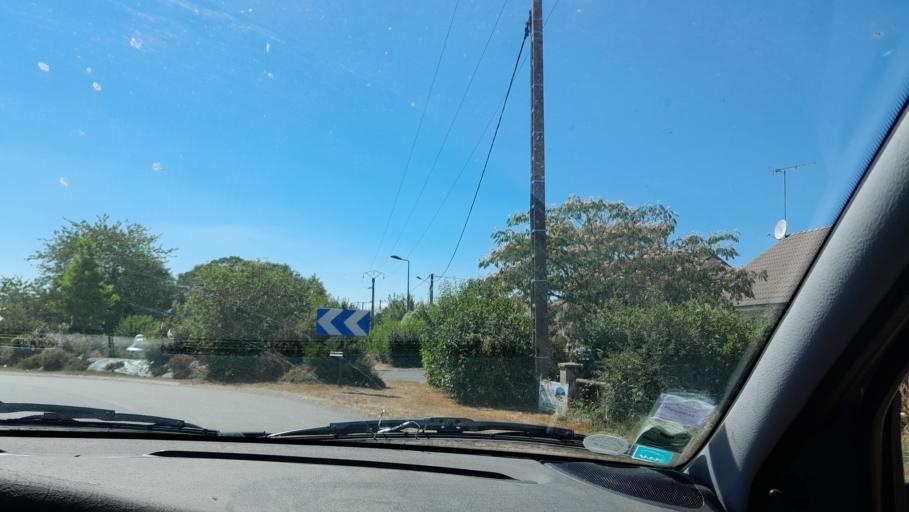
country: FR
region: Pays de la Loire
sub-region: Departement de la Mayenne
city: Congrier
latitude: 47.8306
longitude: -1.1866
